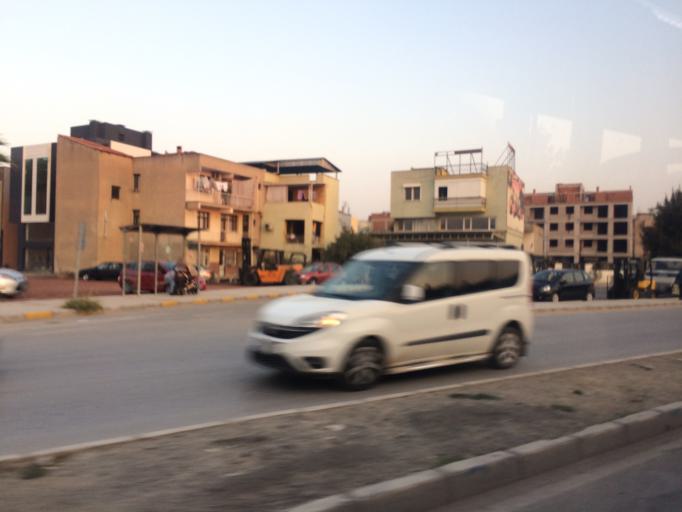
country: TR
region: Izmir
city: Karsiyaka
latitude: 38.4980
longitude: 27.0484
